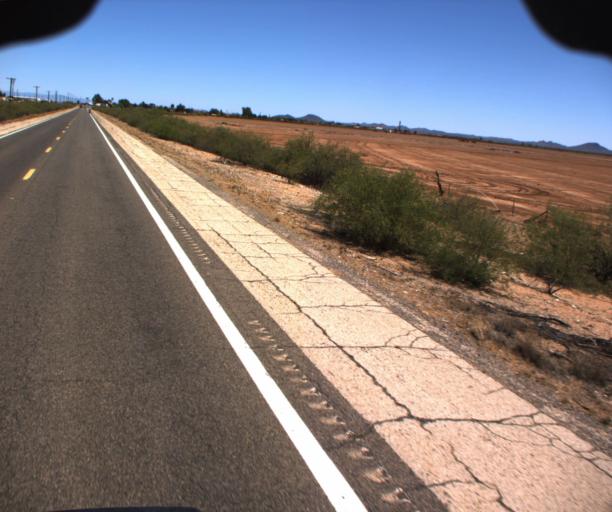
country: US
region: Arizona
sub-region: Yavapai County
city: Congress
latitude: 33.9402
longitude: -113.1875
